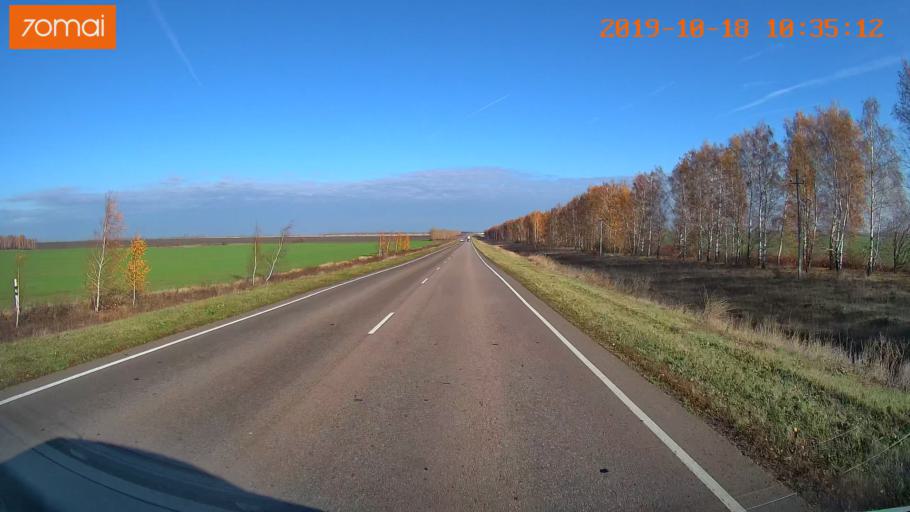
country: RU
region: Tula
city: Kurkino
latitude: 53.5294
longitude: 38.6185
